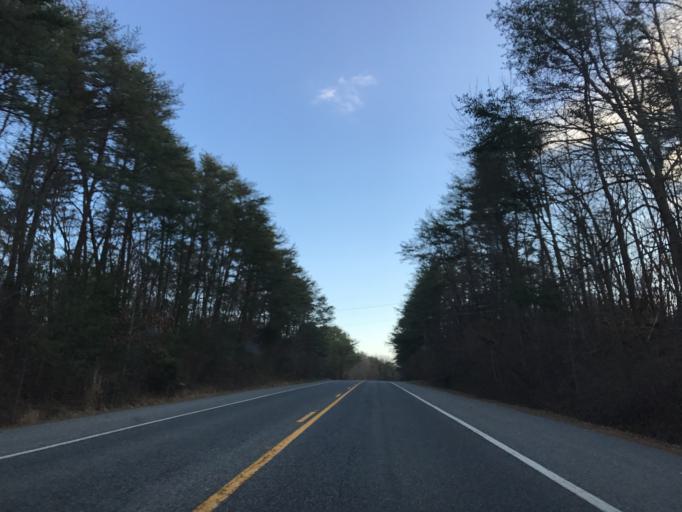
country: US
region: Maryland
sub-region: Cecil County
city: Charlestown
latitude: 39.5545
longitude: -75.9493
